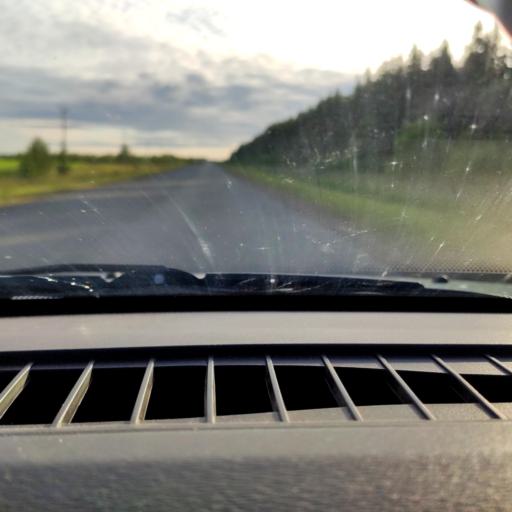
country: RU
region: Perm
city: Uinskoye
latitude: 57.1025
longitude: 56.6558
